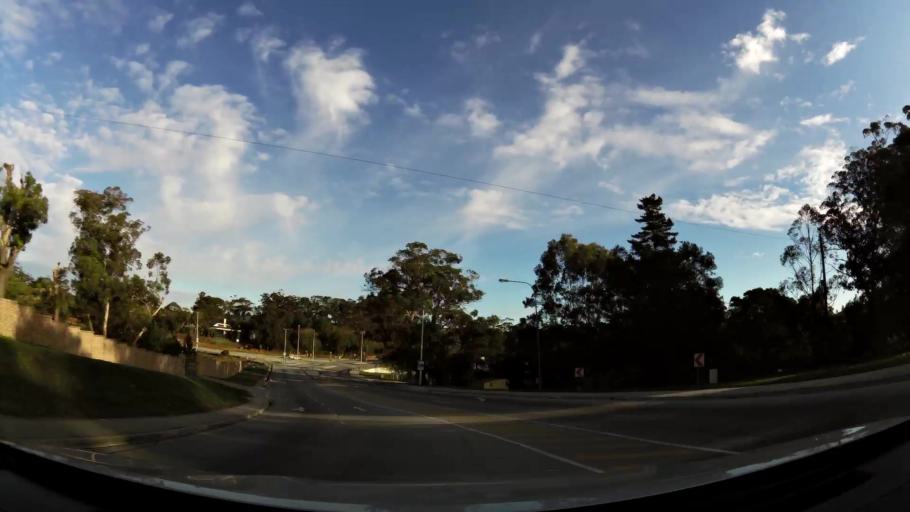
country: ZA
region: Eastern Cape
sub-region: Nelson Mandela Bay Metropolitan Municipality
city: Port Elizabeth
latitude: -33.9576
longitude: 25.5148
